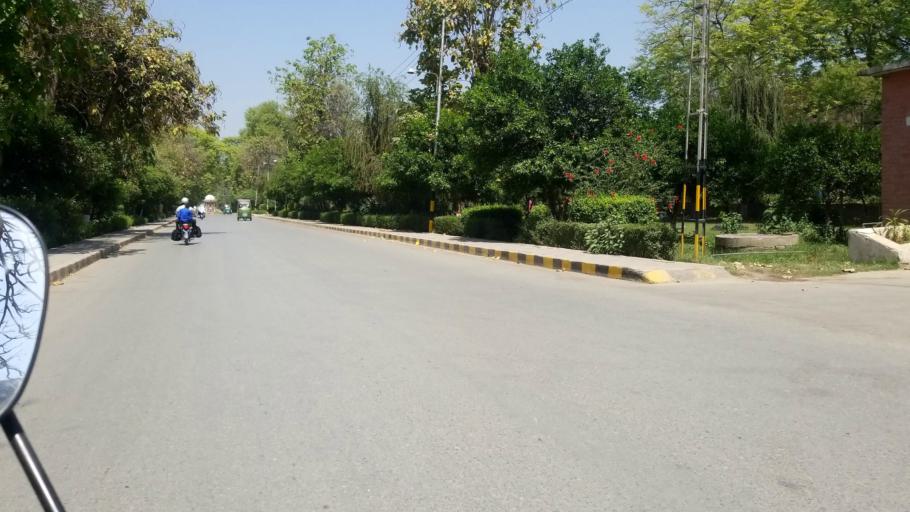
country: PK
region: Khyber Pakhtunkhwa
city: Peshawar
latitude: 34.0057
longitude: 71.4865
